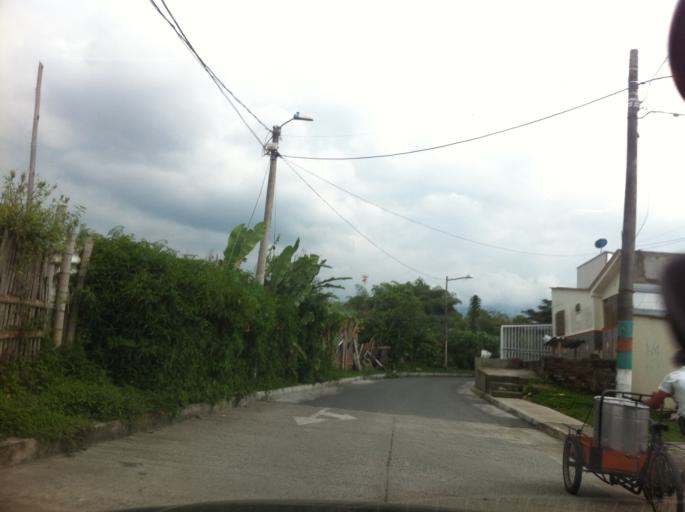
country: CO
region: Quindio
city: Armenia
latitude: 4.5235
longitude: -75.6904
